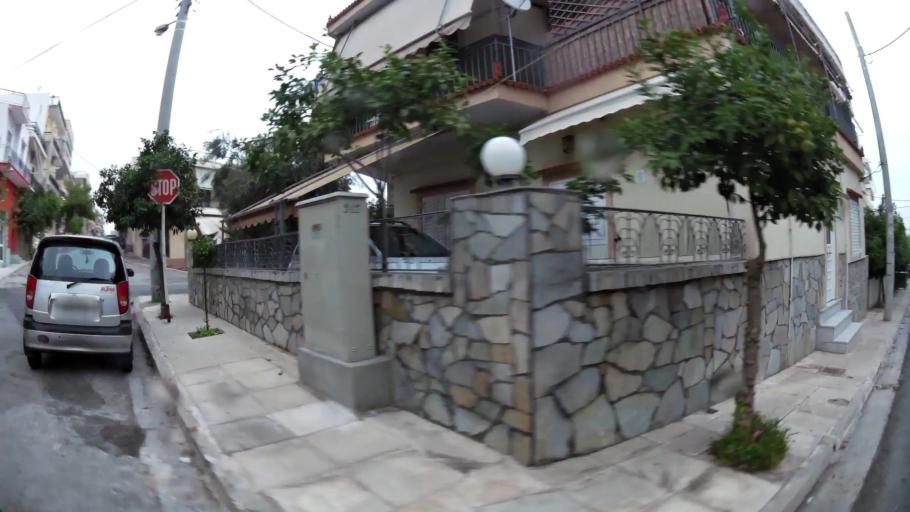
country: GR
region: Attica
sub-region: Nomarchia Athinas
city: Agia Varvara
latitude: 37.9868
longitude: 23.6563
